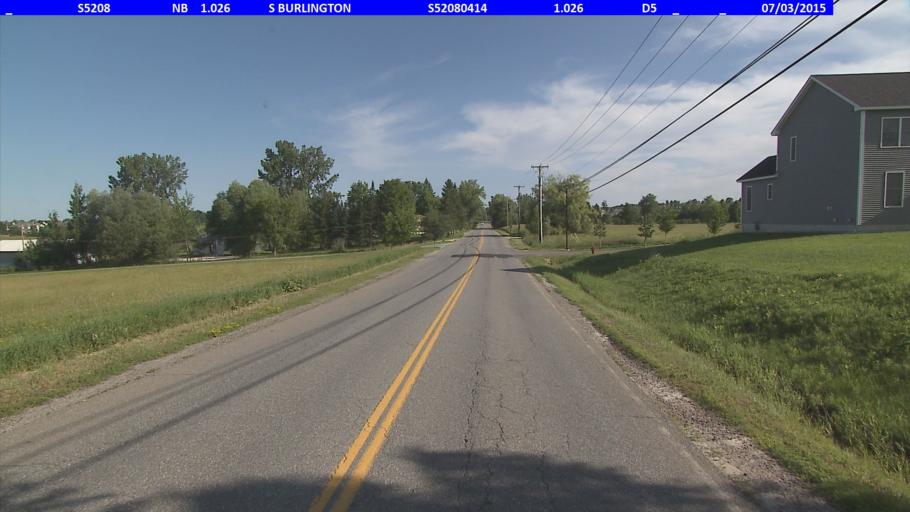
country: US
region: Vermont
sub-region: Chittenden County
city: South Burlington
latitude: 44.4255
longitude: -73.1741
